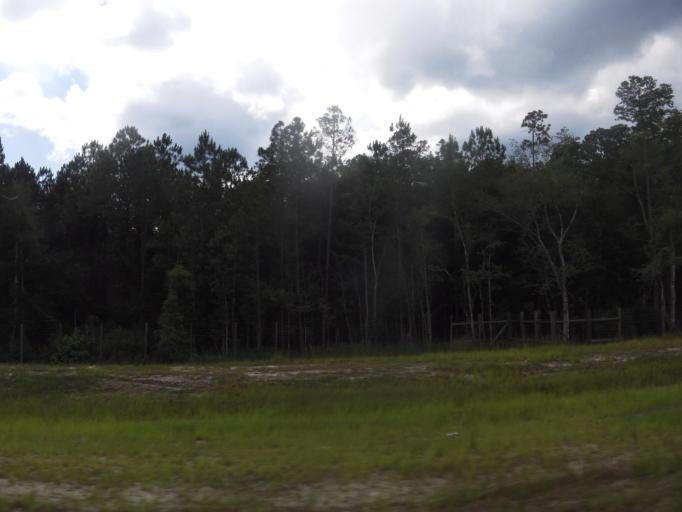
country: US
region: Florida
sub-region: Duval County
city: Baldwin
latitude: 30.3169
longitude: -81.9763
